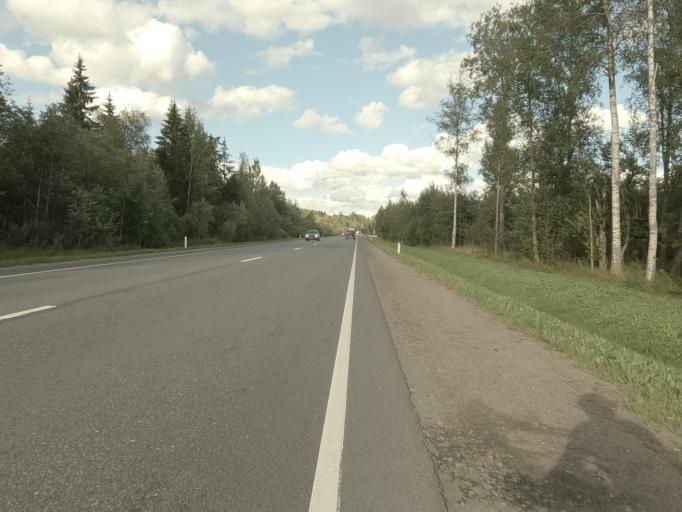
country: RU
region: Leningrad
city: Nikol'skoye
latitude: 59.6637
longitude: 30.8785
